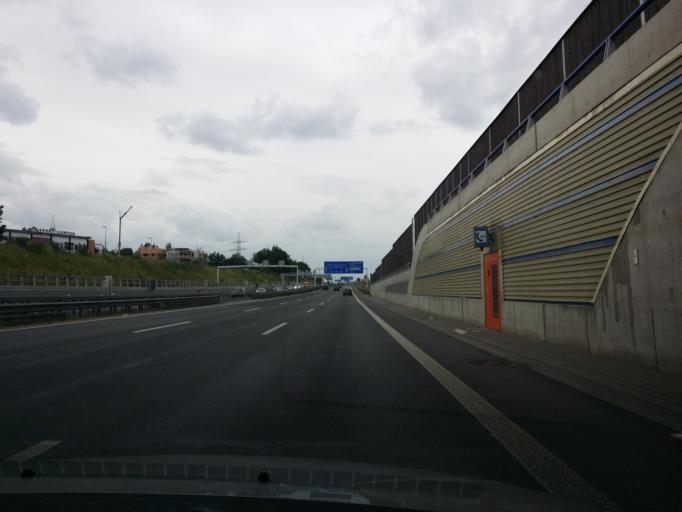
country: DE
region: Rheinland-Pfalz
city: Mainz
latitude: 49.9734
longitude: 8.2736
